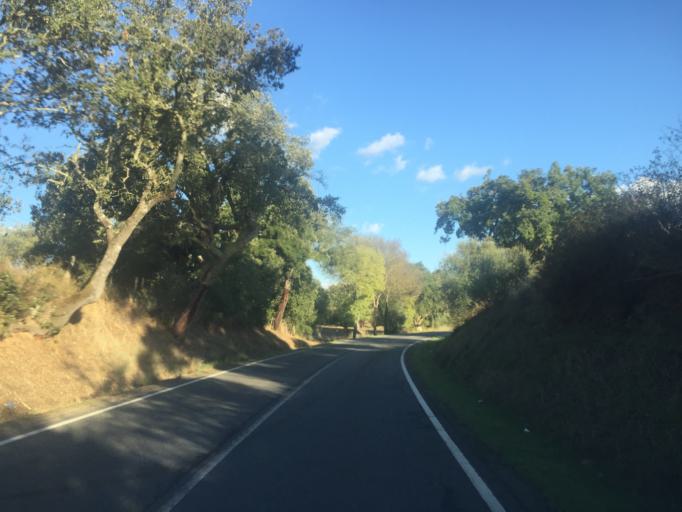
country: PT
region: Portalegre
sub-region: Alter do Chao
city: Alter do Chao
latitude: 39.1967
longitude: -7.6787
